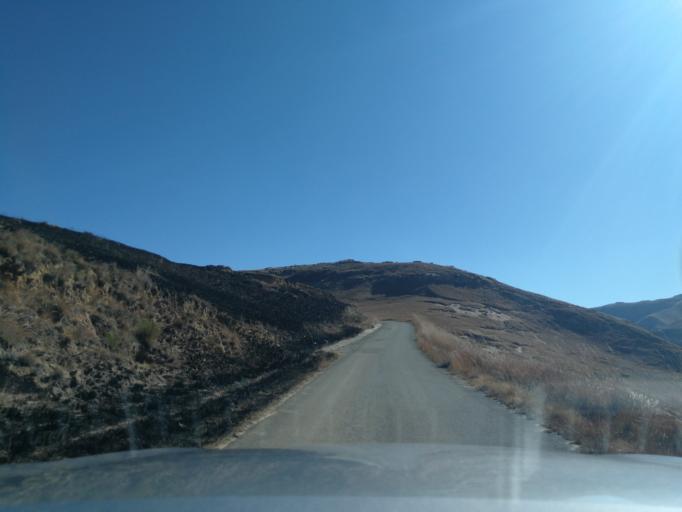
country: ZA
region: Orange Free State
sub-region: Thabo Mofutsanyana District Municipality
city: Phuthaditjhaba
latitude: -28.5117
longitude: 28.6244
